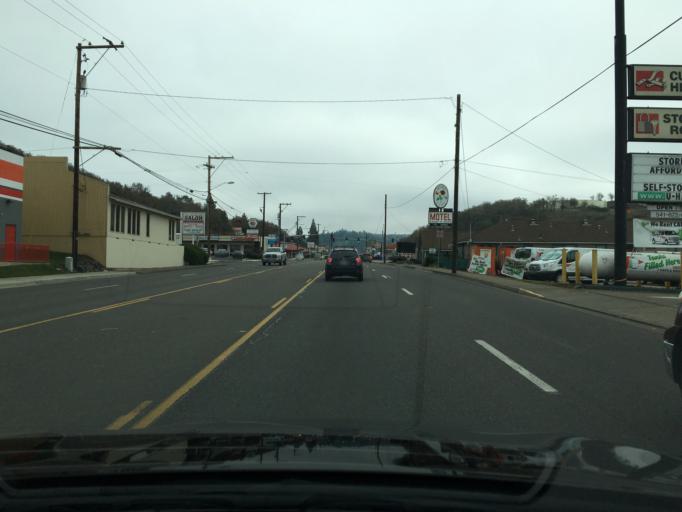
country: US
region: Oregon
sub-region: Douglas County
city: Roseburg
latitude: 43.2246
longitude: -123.3477
